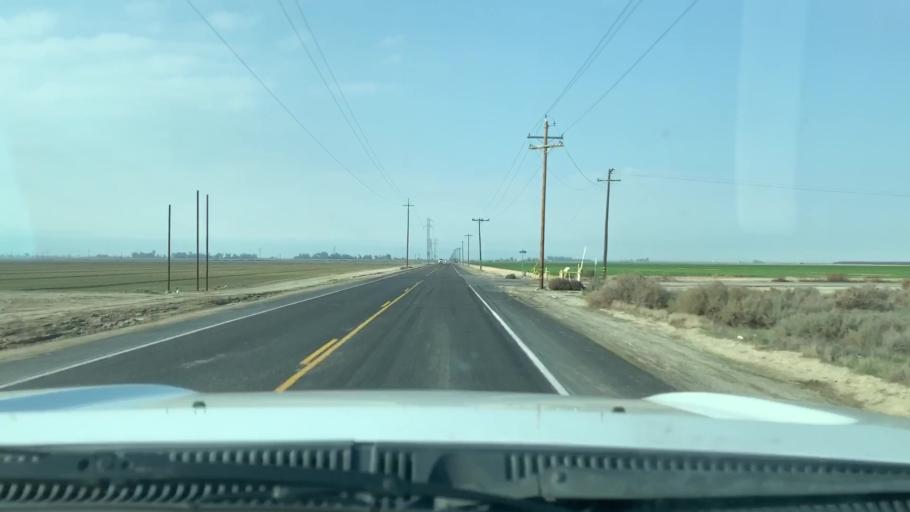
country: US
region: California
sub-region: Kern County
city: Buttonwillow
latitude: 35.4421
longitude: -119.3675
